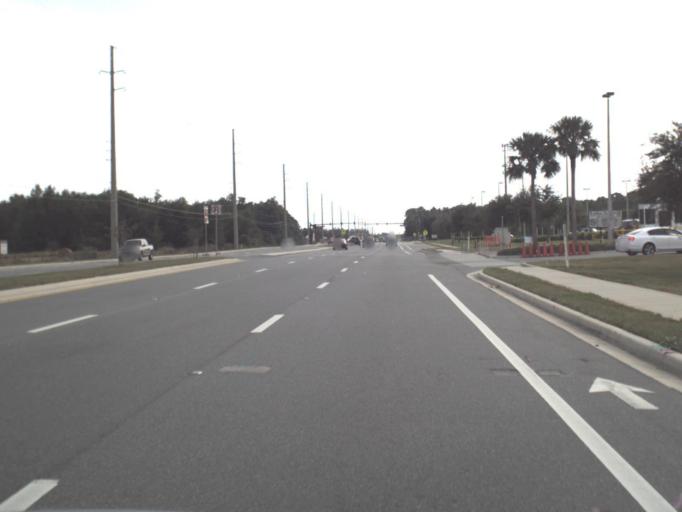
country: US
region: Florida
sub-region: Osceola County
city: Buenaventura Lakes
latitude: 28.3813
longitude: -81.2446
